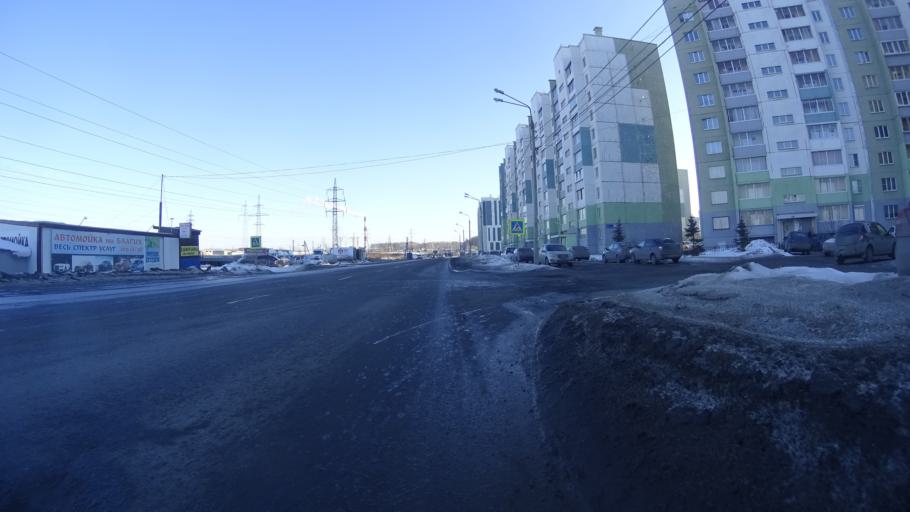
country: RU
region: Chelyabinsk
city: Roshchino
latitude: 55.2160
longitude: 61.3028
